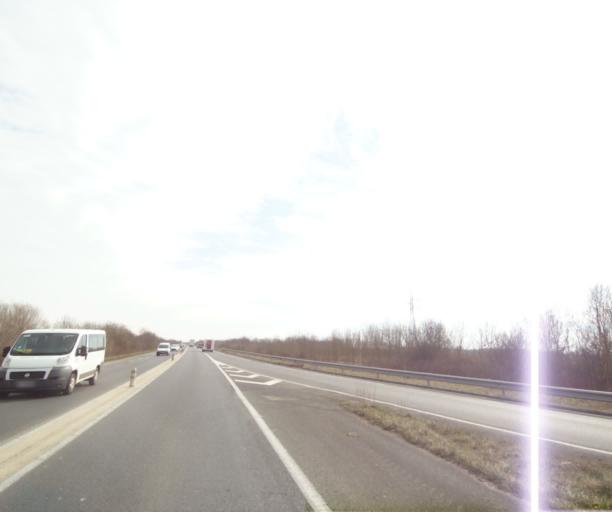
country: FR
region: Poitou-Charentes
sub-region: Departement des Deux-Sevres
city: Niort
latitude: 46.2946
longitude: -0.4642
